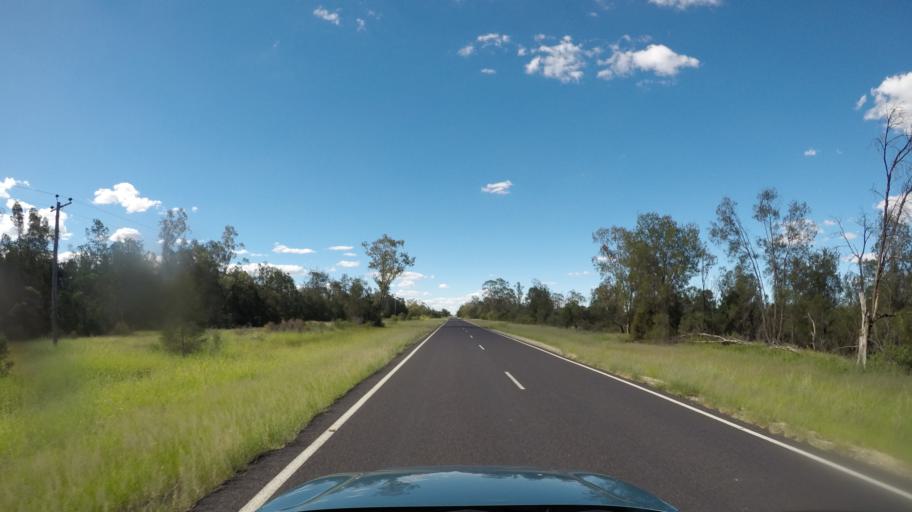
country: AU
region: Queensland
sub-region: Goondiwindi
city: Goondiwindi
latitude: -28.1555
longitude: 150.2878
